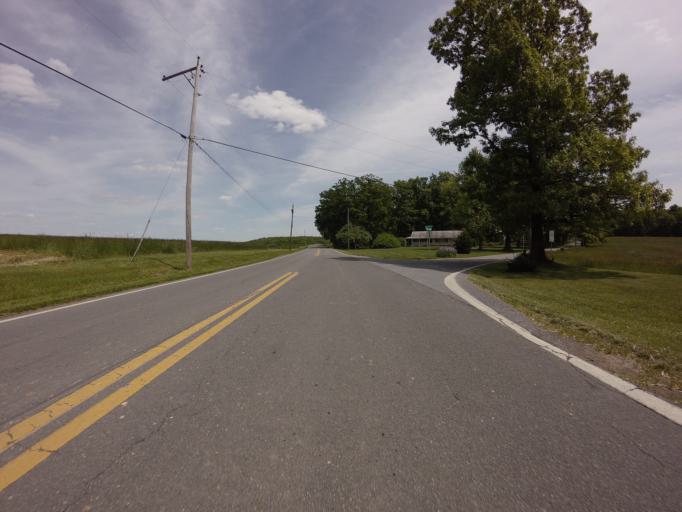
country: US
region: Maryland
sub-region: Frederick County
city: Woodsboro
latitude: 39.5273
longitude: -77.2771
